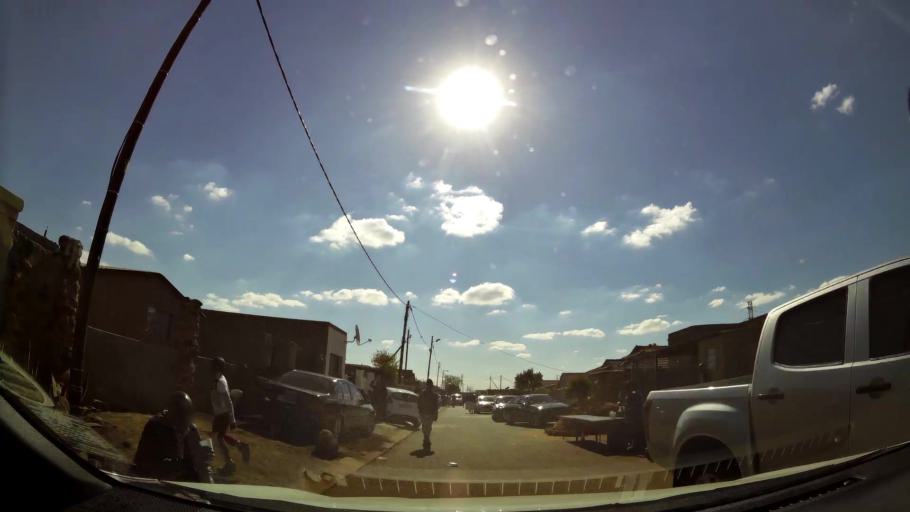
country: ZA
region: Gauteng
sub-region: City of Tshwane Metropolitan Municipality
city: Cullinan
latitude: -25.7167
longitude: 28.4088
